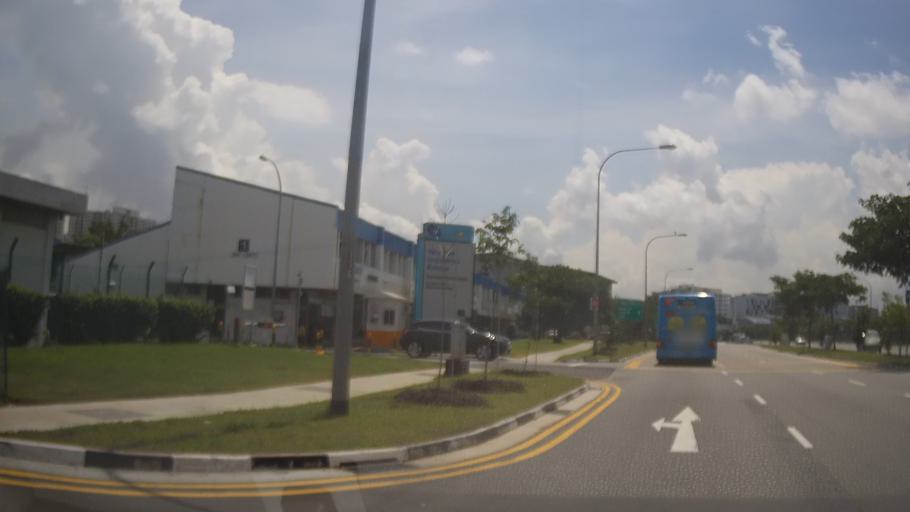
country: MY
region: Johor
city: Johor Bahru
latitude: 1.3967
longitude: 103.7544
